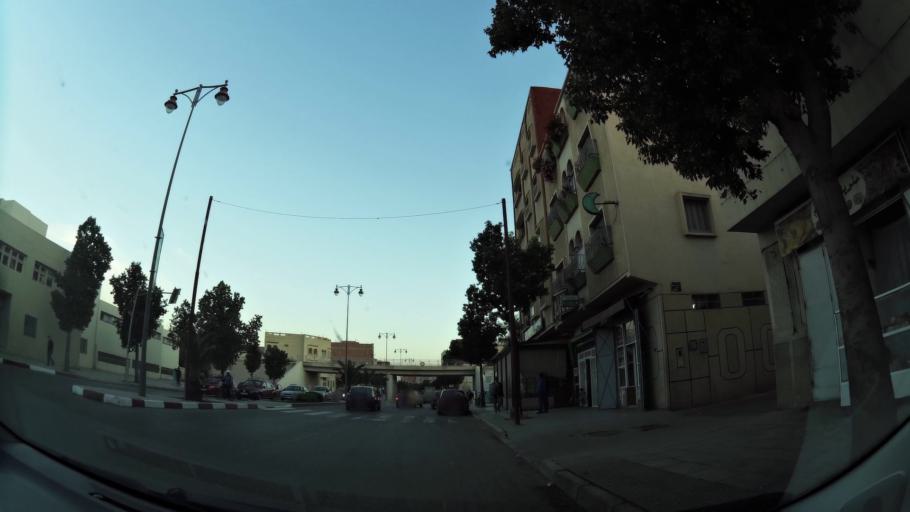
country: MA
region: Oriental
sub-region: Oujda-Angad
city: Oujda
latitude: 34.6972
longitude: -1.9192
